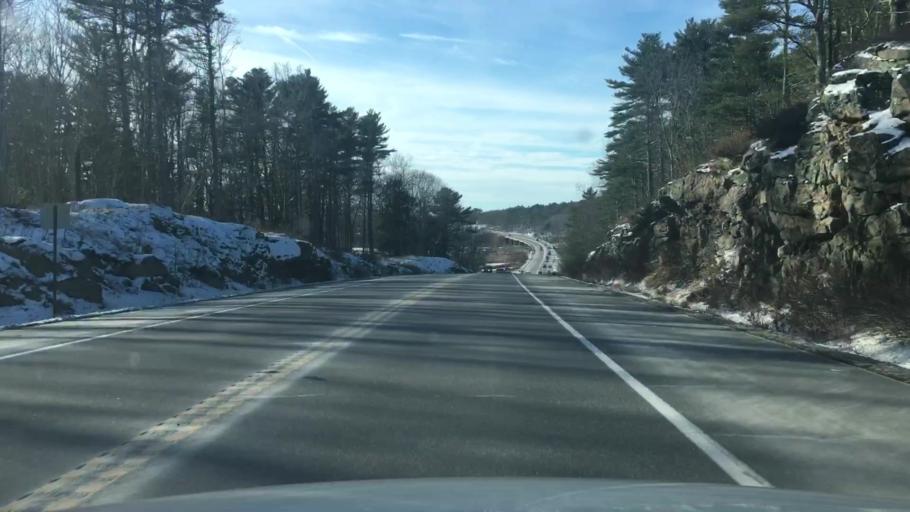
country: US
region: Maine
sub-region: Sagadahoc County
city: Woolwich
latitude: 43.9272
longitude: -69.7892
